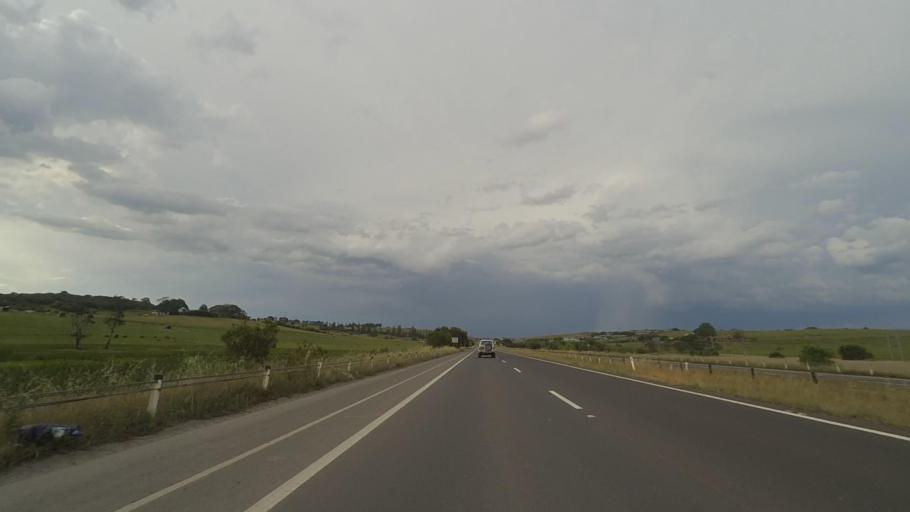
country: AU
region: New South Wales
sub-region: Shellharbour
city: Croom
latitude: -34.6023
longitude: 150.8403
